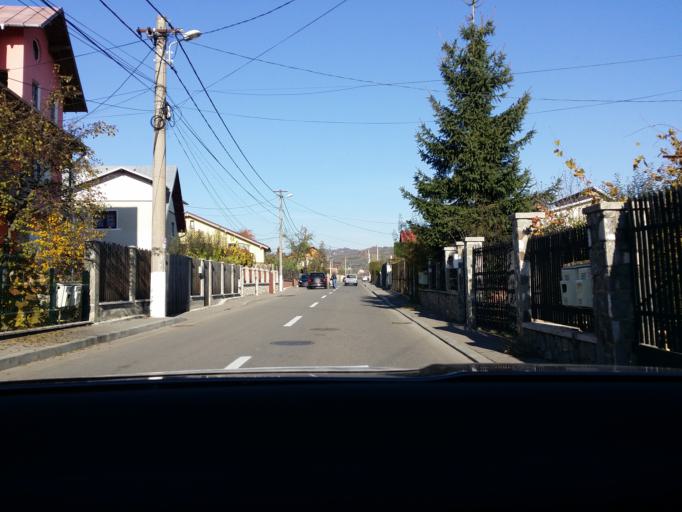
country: RO
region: Prahova
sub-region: Municipiul Campina
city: Campina
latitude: 45.1401
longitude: 25.7293
